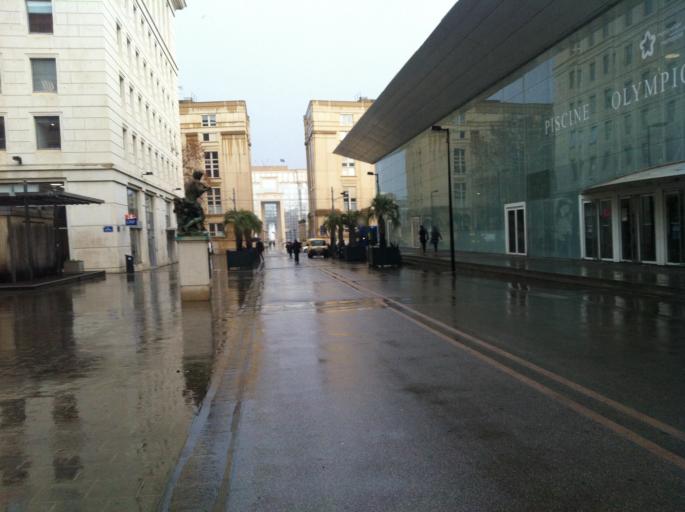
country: FR
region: Languedoc-Roussillon
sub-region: Departement de l'Herault
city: Montpellier
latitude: 43.6078
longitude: 3.8930
